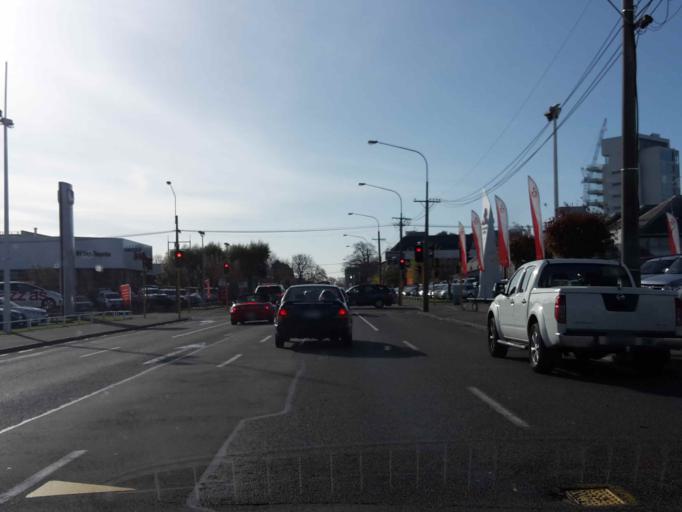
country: NZ
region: Canterbury
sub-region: Christchurch City
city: Christchurch
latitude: -43.5371
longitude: 172.6306
